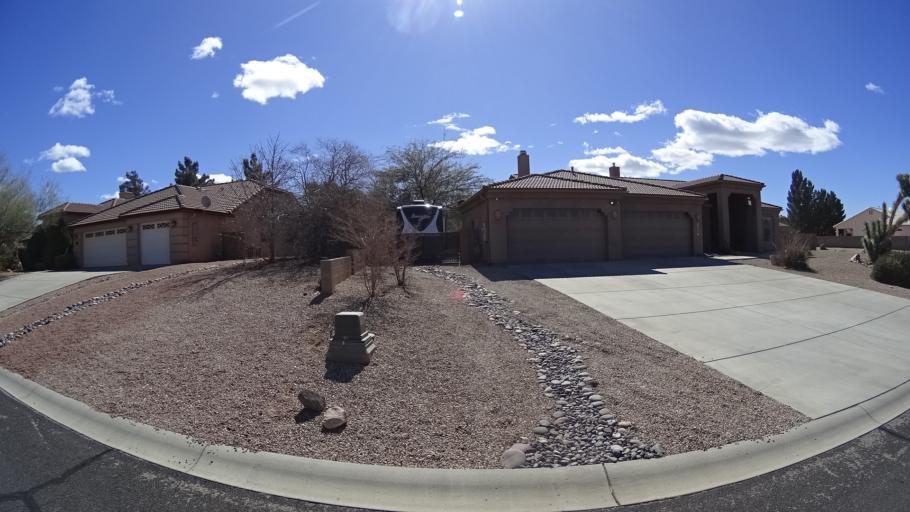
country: US
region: Arizona
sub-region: Mohave County
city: Kingman
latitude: 35.2052
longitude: -113.9727
